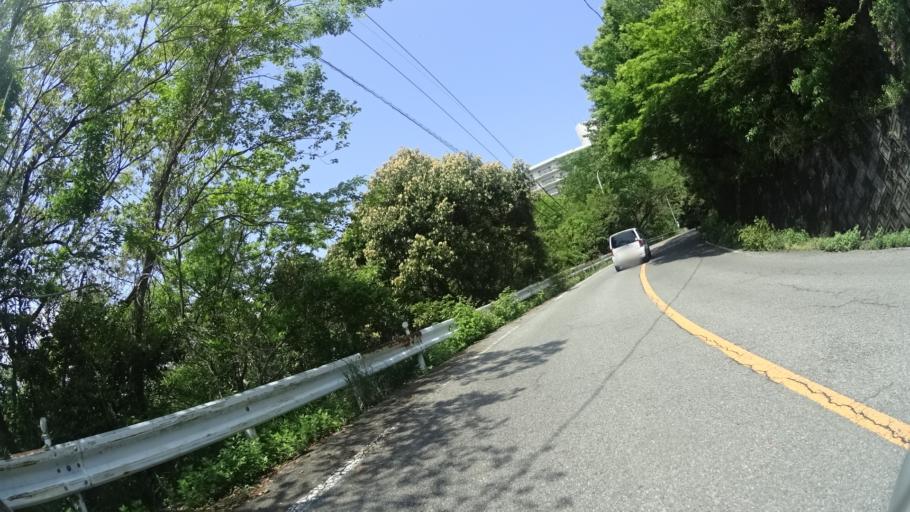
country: JP
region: Tokushima
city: Tokushima-shi
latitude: 34.0659
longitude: 134.5319
